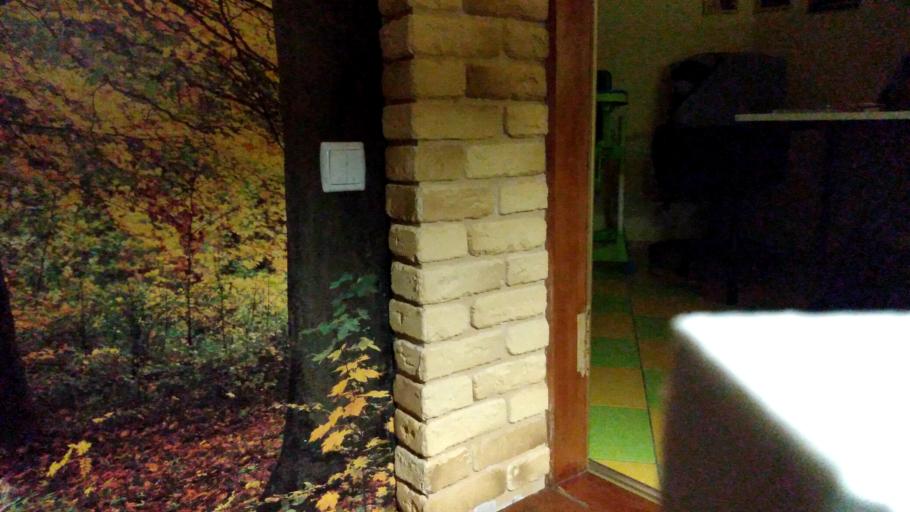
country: RU
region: Vologda
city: Lipin Bor
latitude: 60.8714
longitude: 38.0073
